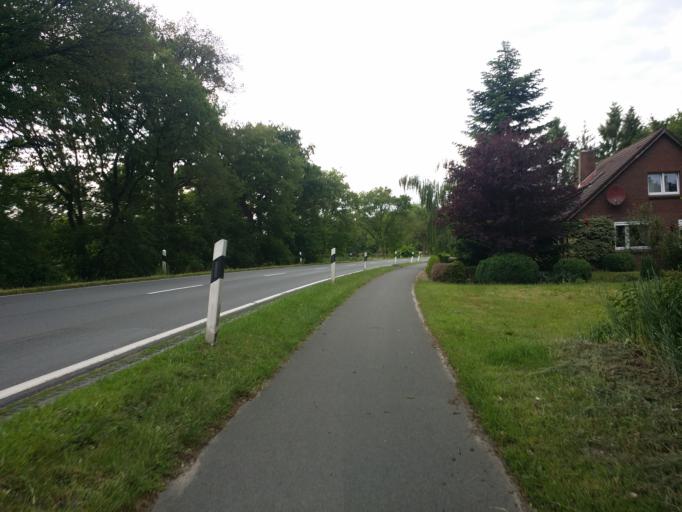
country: DE
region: Lower Saxony
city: Wittmund
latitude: 53.5125
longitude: 7.7959
